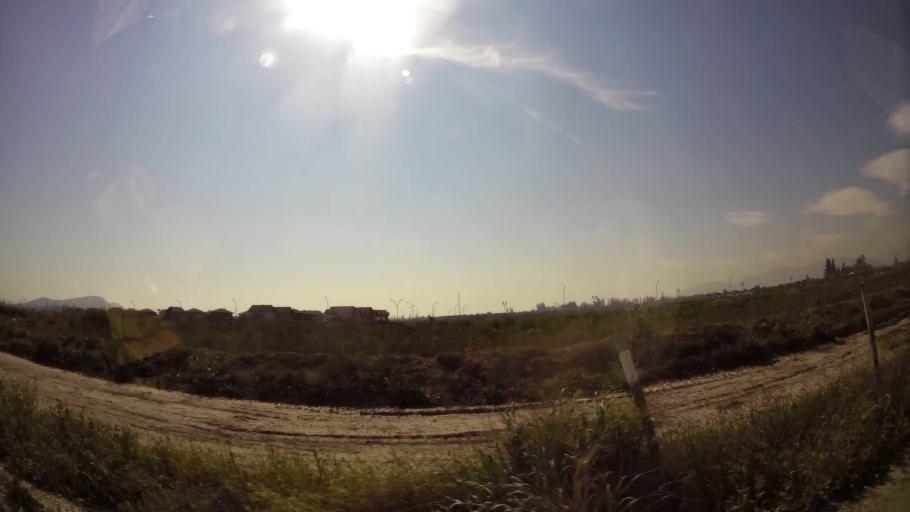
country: CL
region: Santiago Metropolitan
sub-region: Provincia de Talagante
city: Penaflor
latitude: -33.5675
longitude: -70.8318
